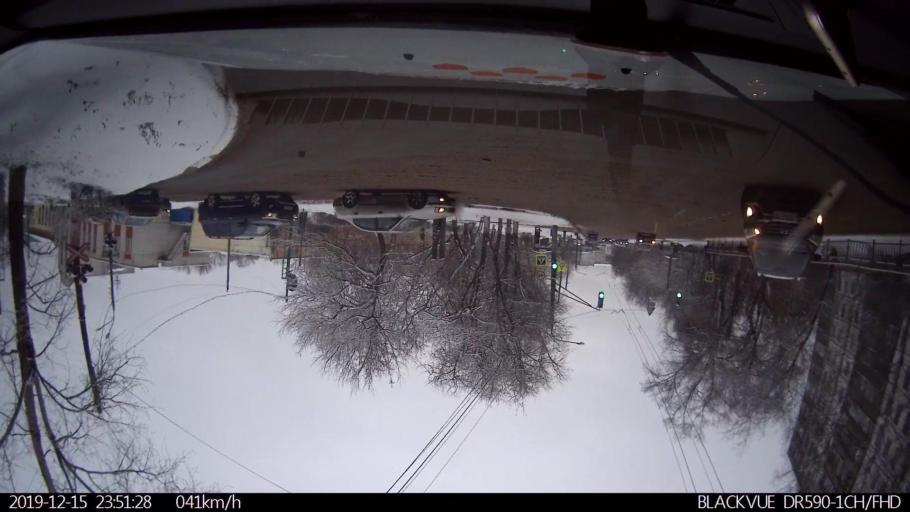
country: RU
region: Nizjnij Novgorod
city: Nizhniy Novgorod
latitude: 56.2743
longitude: 43.9366
